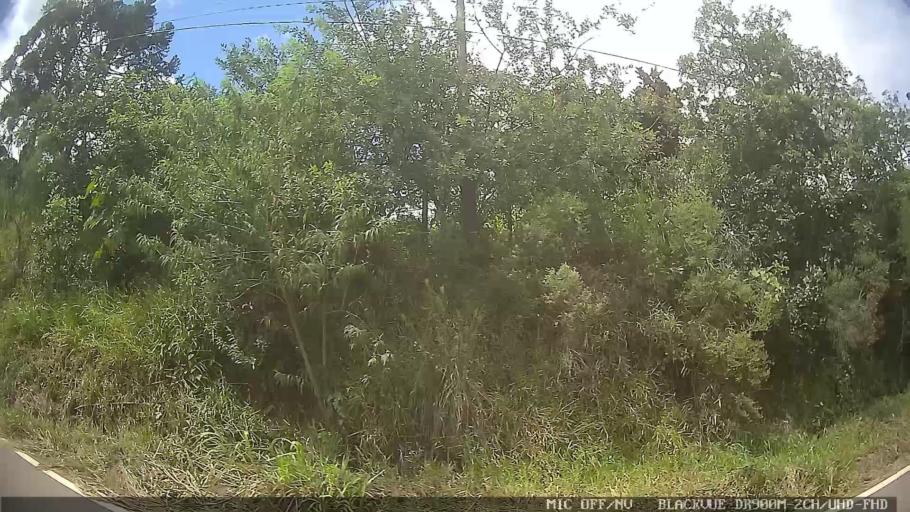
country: BR
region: Minas Gerais
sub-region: Extrema
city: Extrema
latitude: -22.8064
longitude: -46.4521
